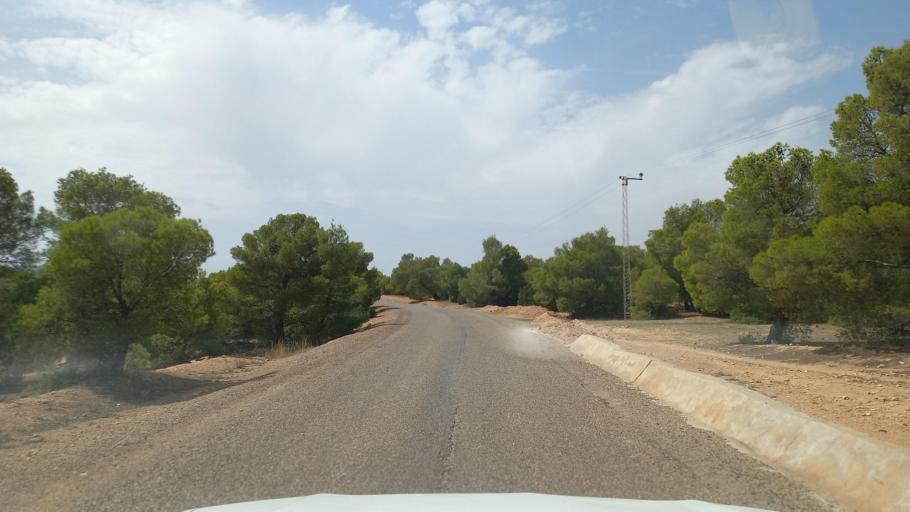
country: TN
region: Al Qasrayn
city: Kasserine
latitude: 35.3755
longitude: 8.9054
